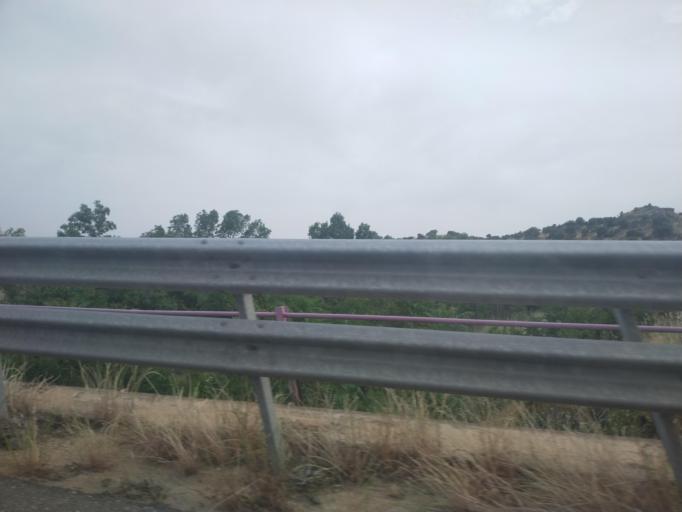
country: ES
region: Castille-La Mancha
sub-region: Province of Toledo
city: Layos
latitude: 39.8154
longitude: -4.0978
